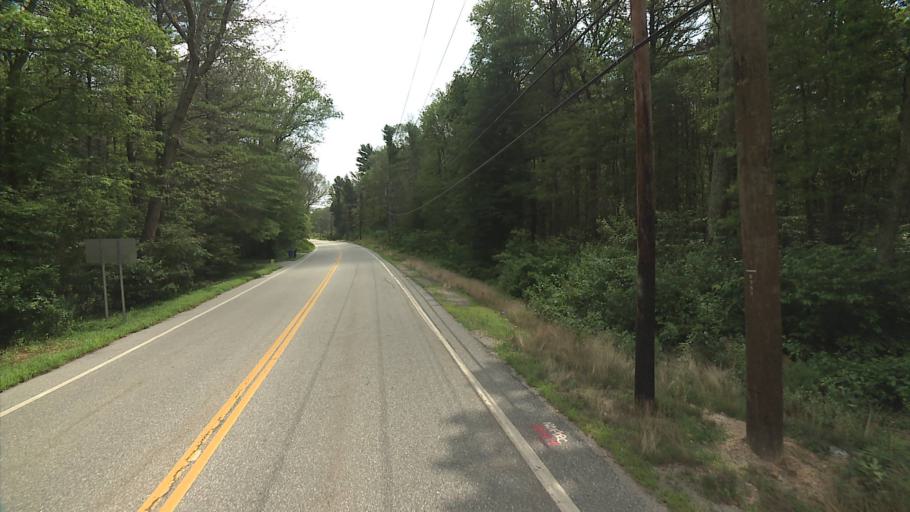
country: US
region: Rhode Island
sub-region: Washington County
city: Hopkinton
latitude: 41.5733
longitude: -71.8329
